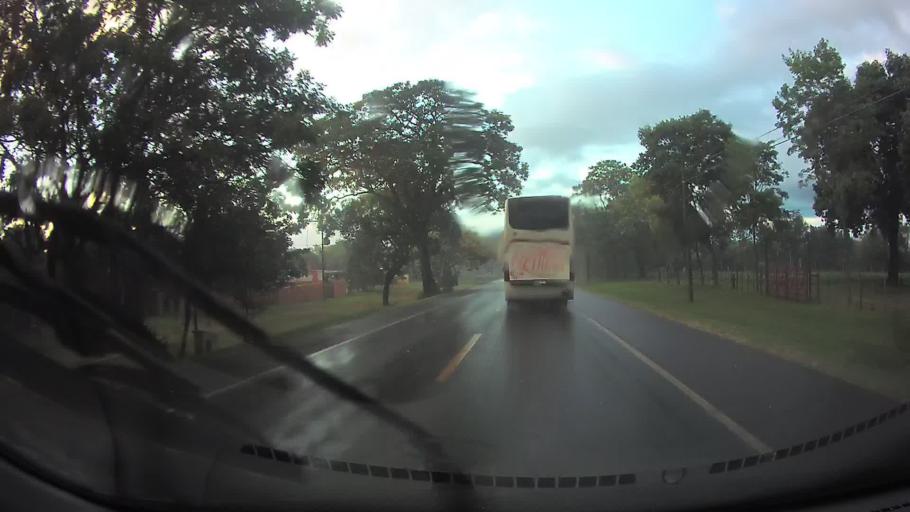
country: PY
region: Paraguari
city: Yaguaron
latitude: -25.5776
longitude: -57.2589
